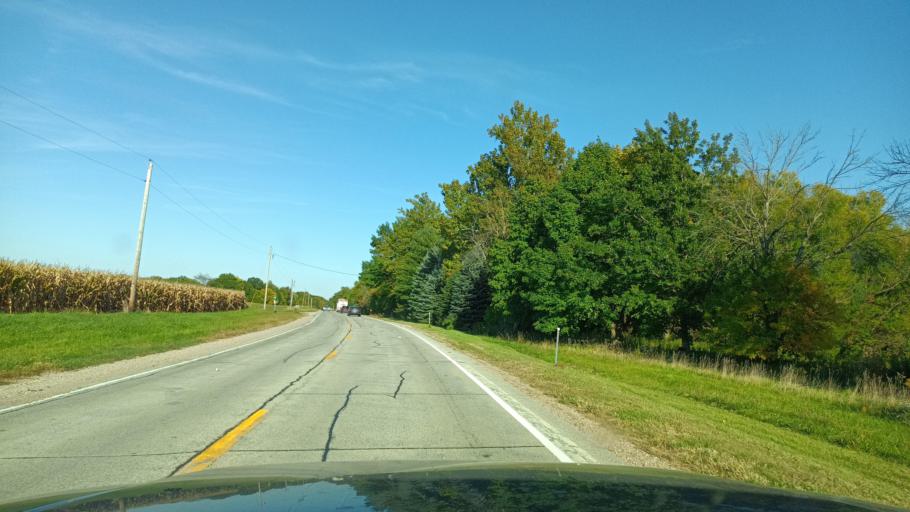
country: US
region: Illinois
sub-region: De Witt County
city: Farmer City
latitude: 40.2241
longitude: -88.6951
